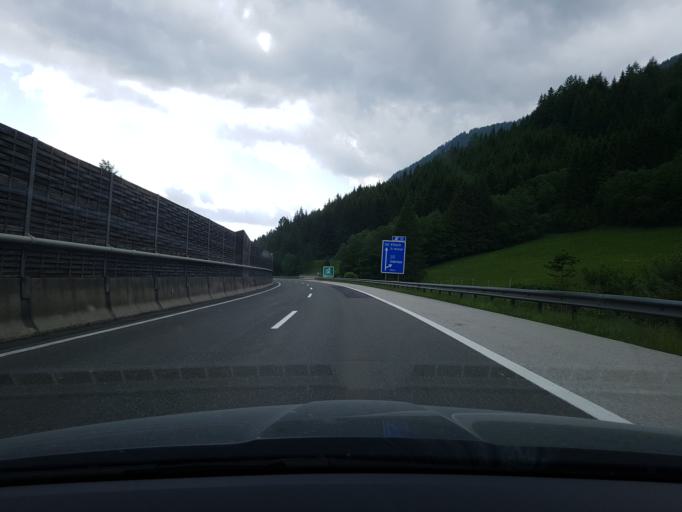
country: AT
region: Salzburg
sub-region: Politischer Bezirk Tamsweg
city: Zederhaus
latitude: 47.1645
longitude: 13.4683
